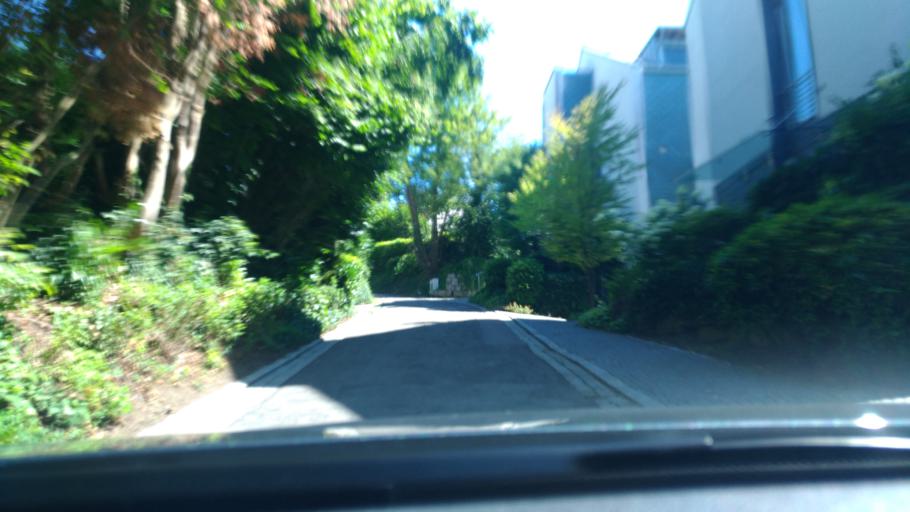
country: DE
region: Baden-Wuerttemberg
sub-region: Tuebingen Region
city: Uberlingen
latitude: 47.7730
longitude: 9.1375
